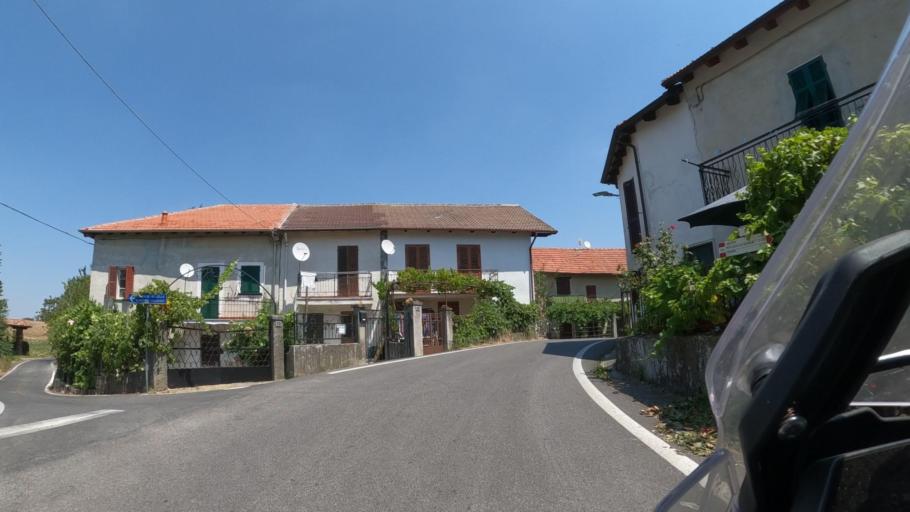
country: IT
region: Piedmont
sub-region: Provincia di Alessandria
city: Ponzone
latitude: 44.5535
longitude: 8.4845
